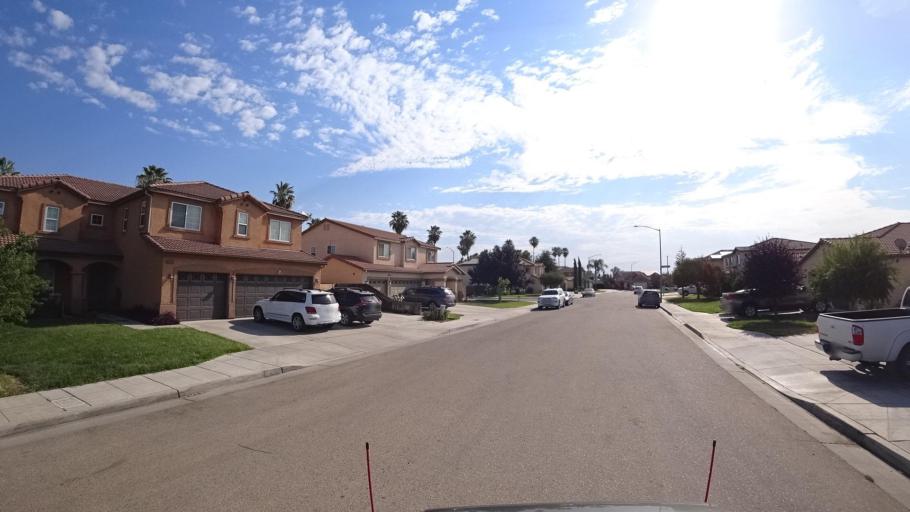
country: US
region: California
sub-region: Fresno County
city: Sunnyside
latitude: 36.7191
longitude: -119.7019
